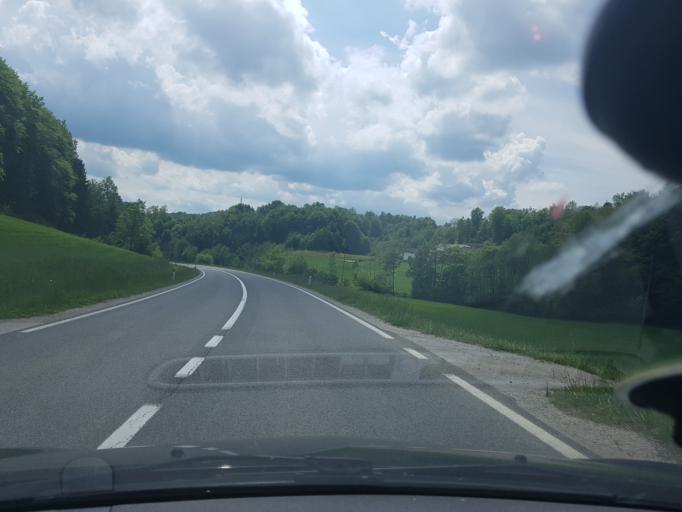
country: SI
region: Rogaska Slatina
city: Rogaska Slatina
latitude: 46.2495
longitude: 15.6045
